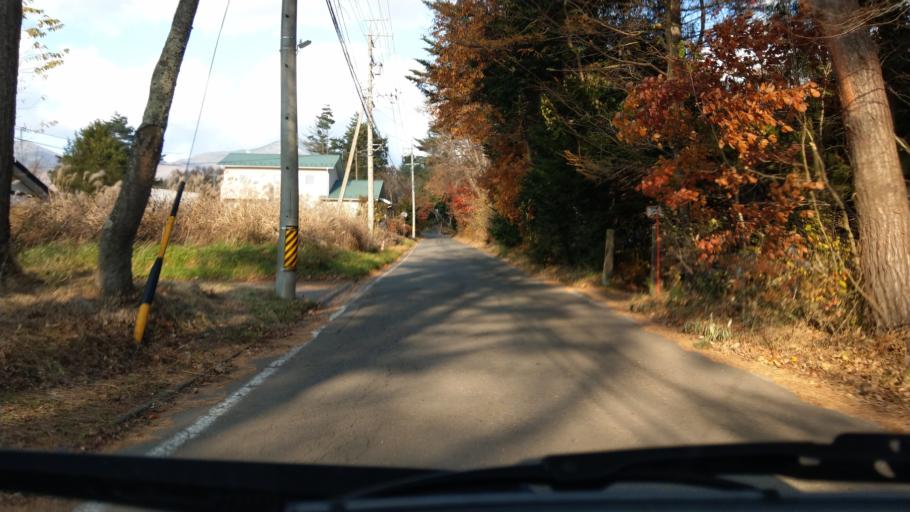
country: JP
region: Nagano
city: Komoro
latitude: 36.3490
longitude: 138.4572
